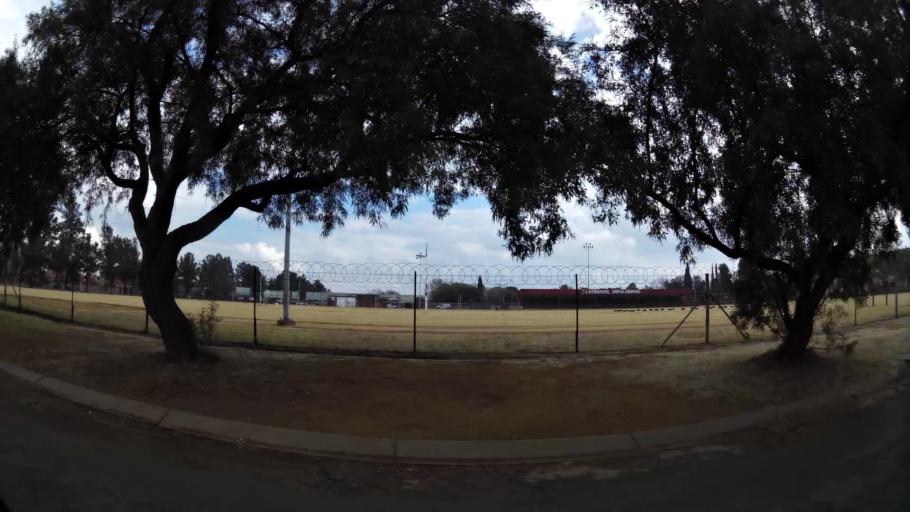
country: ZA
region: Gauteng
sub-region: Sedibeng District Municipality
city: Vanderbijlpark
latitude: -26.7377
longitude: 27.8492
